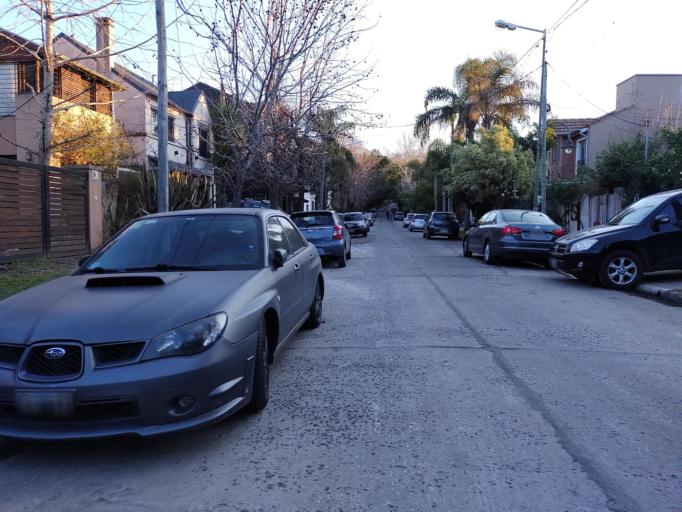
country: AR
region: Buenos Aires
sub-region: Partido de San Isidro
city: San Isidro
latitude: -34.4458
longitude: -58.5339
